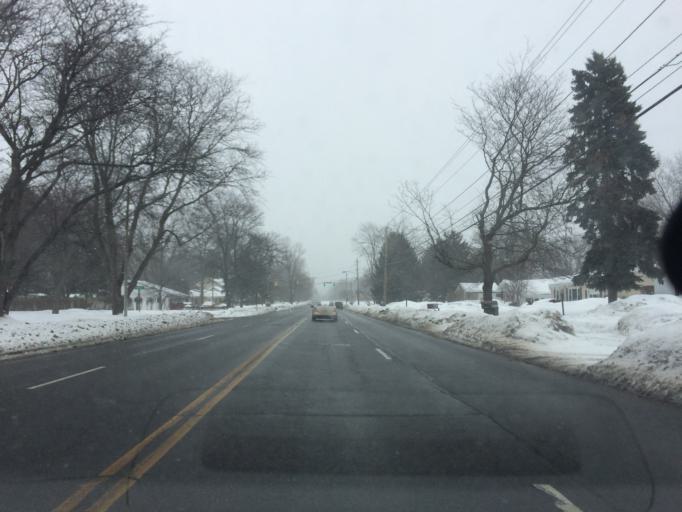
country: US
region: New York
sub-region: Monroe County
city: Brighton
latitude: 43.1258
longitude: -77.5845
